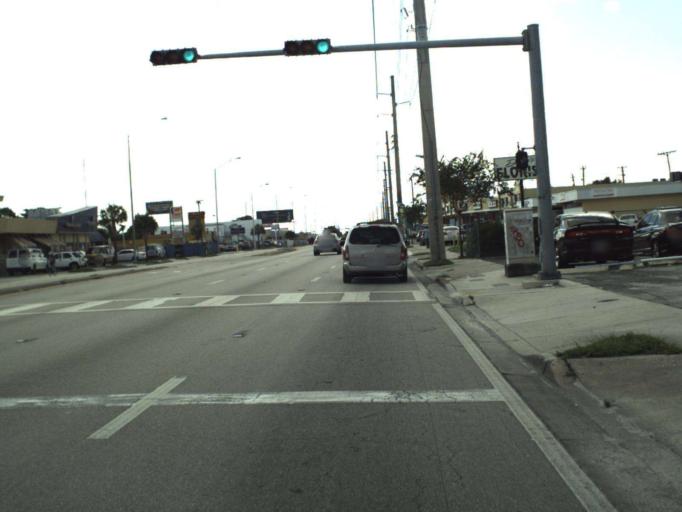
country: US
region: Florida
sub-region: Miami-Dade County
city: Golden Glades
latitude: 25.9099
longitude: -80.2118
